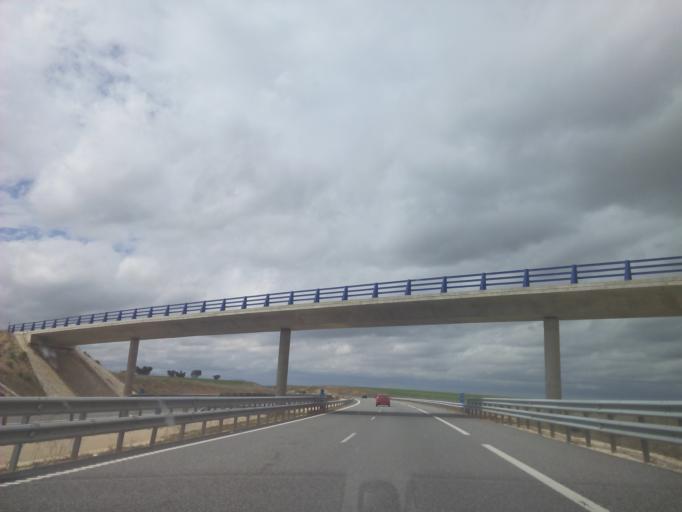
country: ES
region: Castille and Leon
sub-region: Provincia de Salamanca
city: Machacon
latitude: 40.9267
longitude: -5.5386
